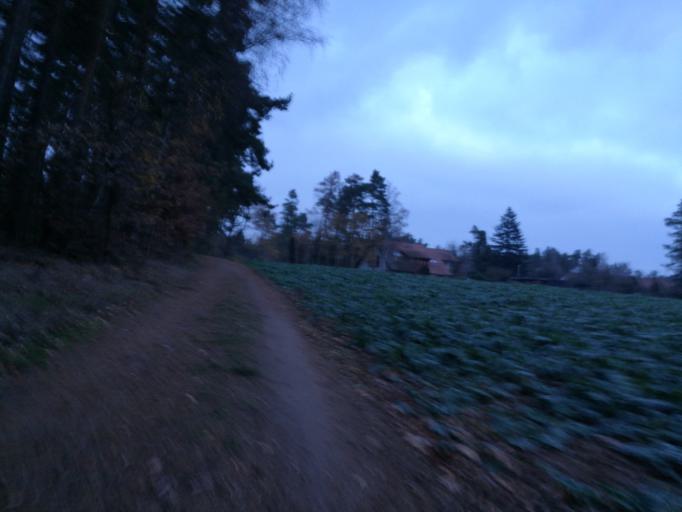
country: DE
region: Bavaria
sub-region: Regierungsbezirk Mittelfranken
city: Seukendorf
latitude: 49.4694
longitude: 10.8820
